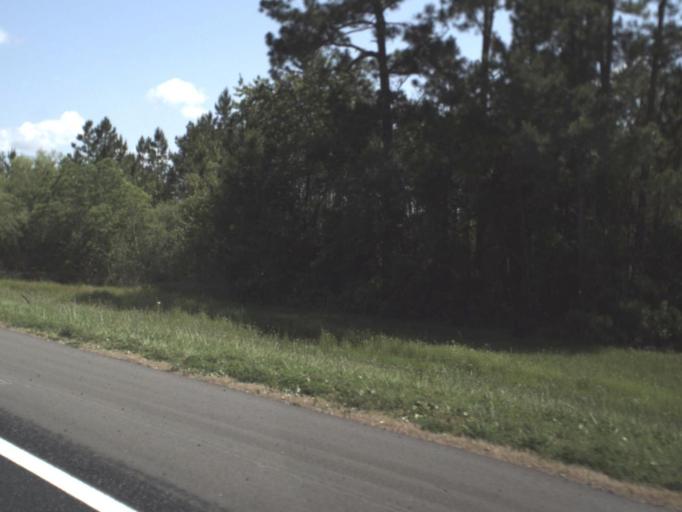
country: US
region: Florida
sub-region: Nassau County
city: Yulee
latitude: 30.6065
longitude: -81.6453
